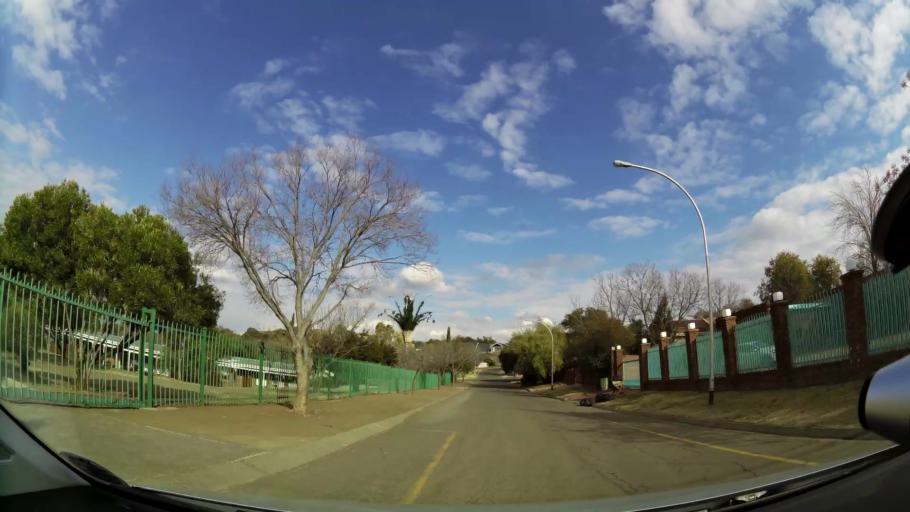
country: ZA
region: Orange Free State
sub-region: Mangaung Metropolitan Municipality
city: Bloemfontein
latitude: -29.0774
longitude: 26.2315
